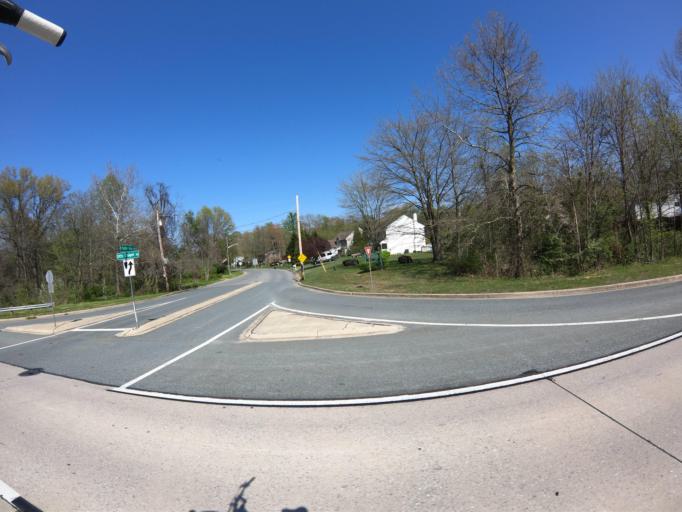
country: US
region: Delaware
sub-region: New Castle County
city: Newark
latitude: 39.6512
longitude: -75.7803
